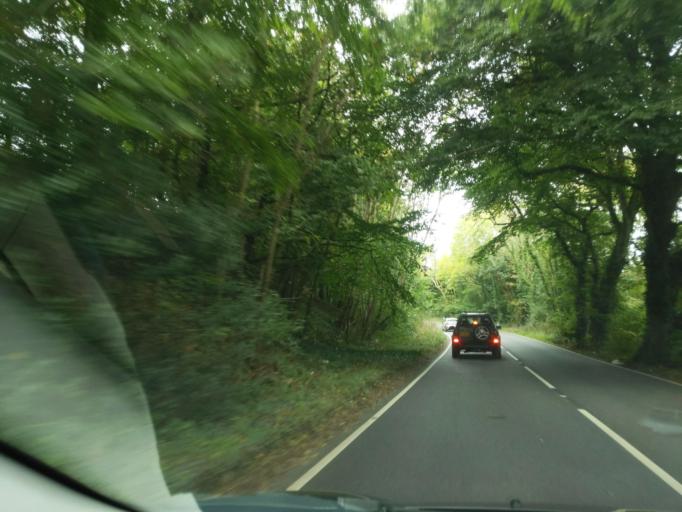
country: GB
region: England
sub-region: Cornwall
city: Helland
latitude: 50.5022
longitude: -4.7763
